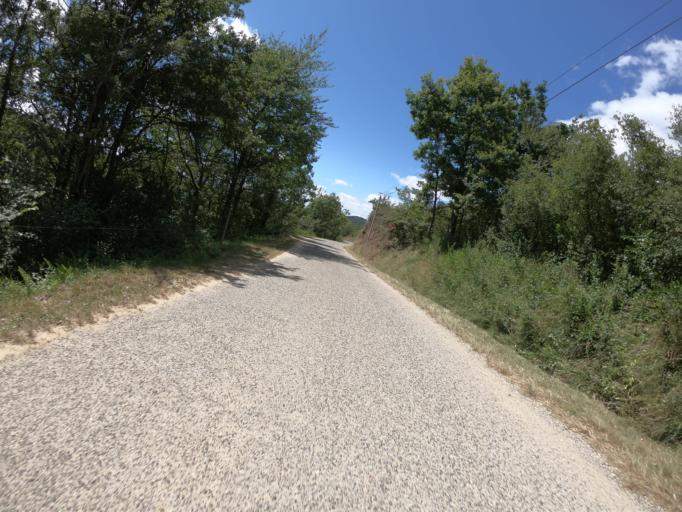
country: FR
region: Midi-Pyrenees
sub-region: Departement de l'Ariege
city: Mirepoix
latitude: 43.0474
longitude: 1.8311
